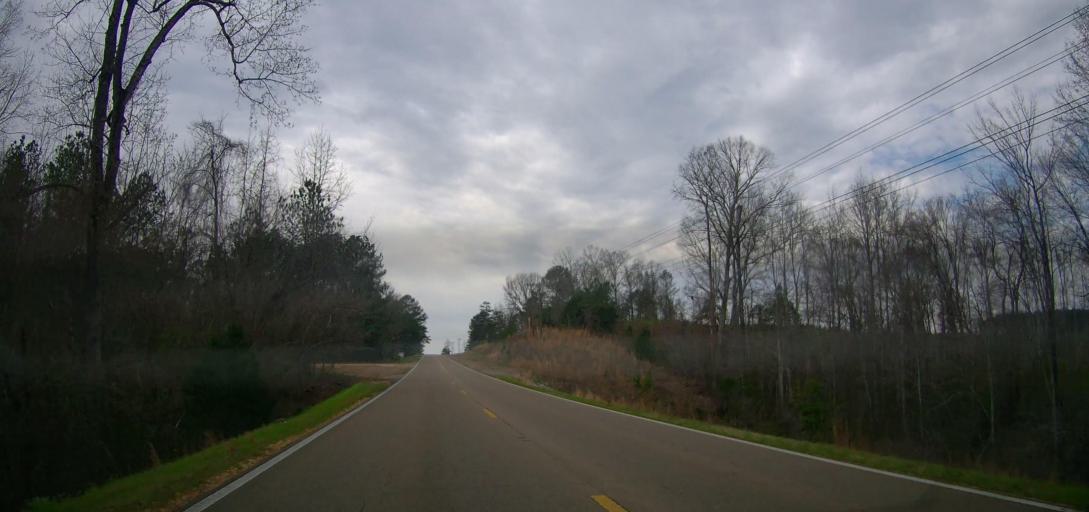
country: US
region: Mississippi
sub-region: Itawamba County
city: Fulton
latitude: 34.2758
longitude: -88.3544
